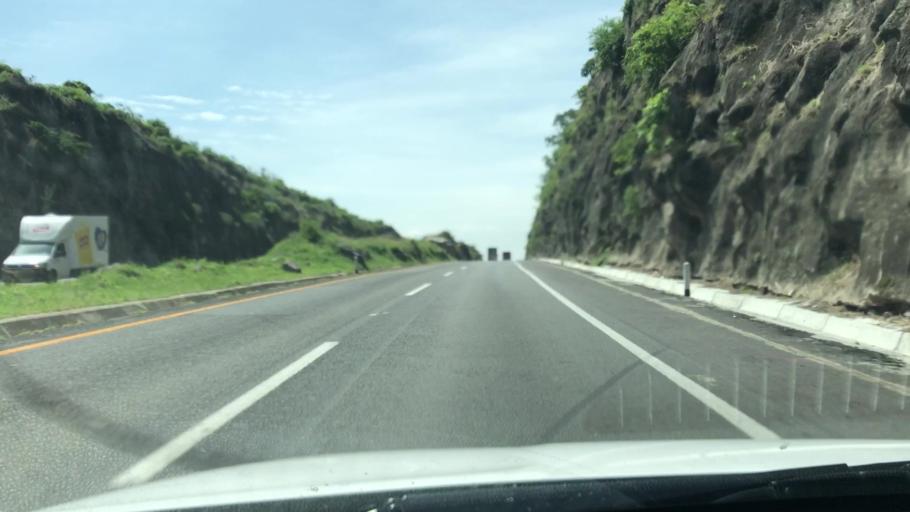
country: MX
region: Jalisco
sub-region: Zapotlan del Rey
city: Zapotlan del Rey
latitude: 20.5155
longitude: -102.9755
